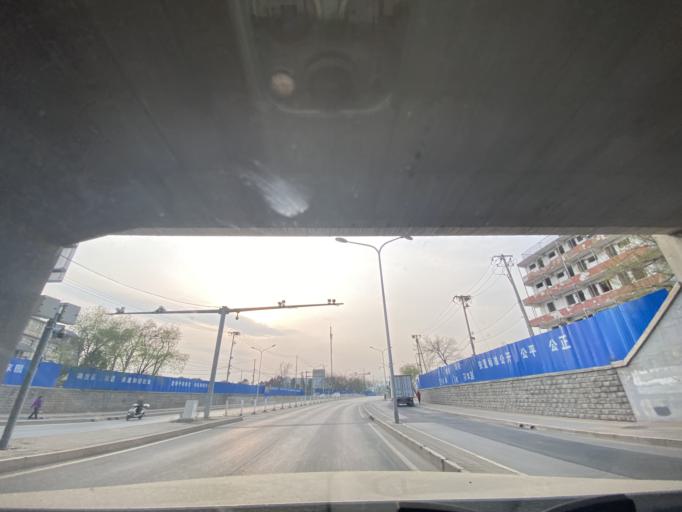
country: CN
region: Beijing
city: Babaoshan
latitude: 39.9286
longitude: 116.2318
